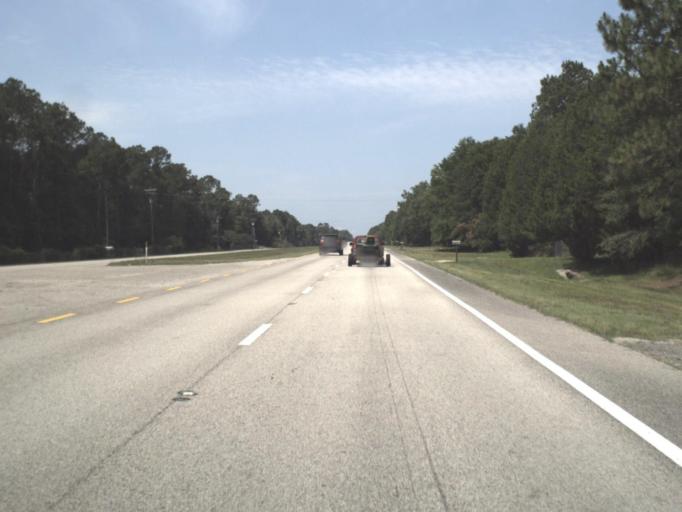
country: US
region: Florida
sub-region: Alachua County
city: Waldo
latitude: 29.7351
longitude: -82.2429
